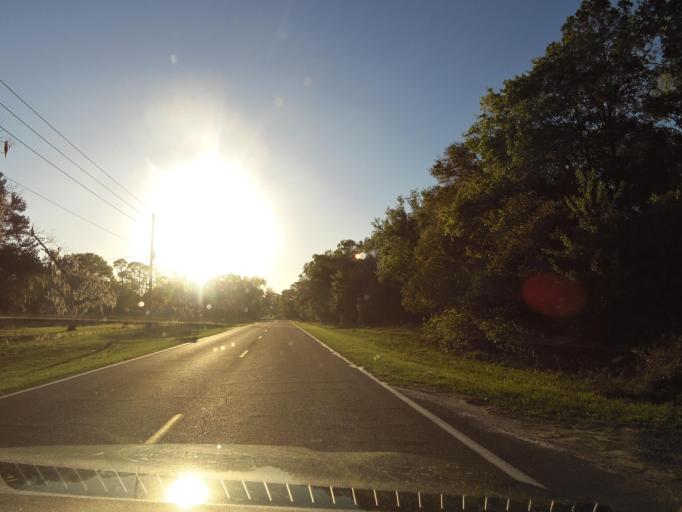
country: US
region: Florida
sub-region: Bradford County
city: Starke
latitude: 29.8646
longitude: -82.1283
